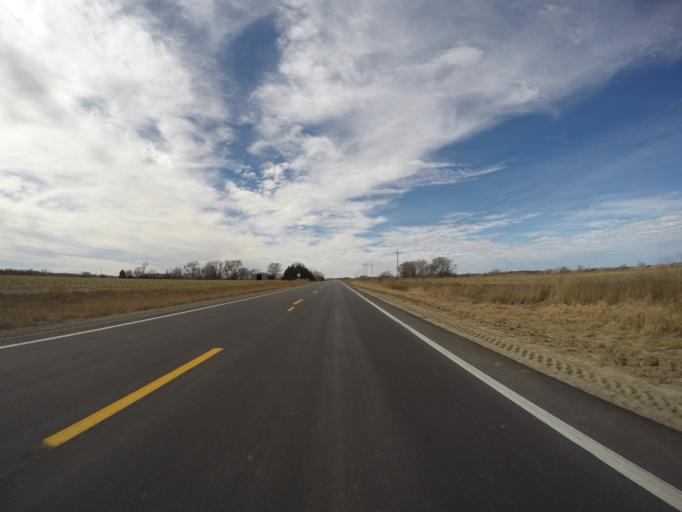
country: US
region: Nebraska
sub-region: Franklin County
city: Franklin
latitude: 40.0964
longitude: -98.8374
